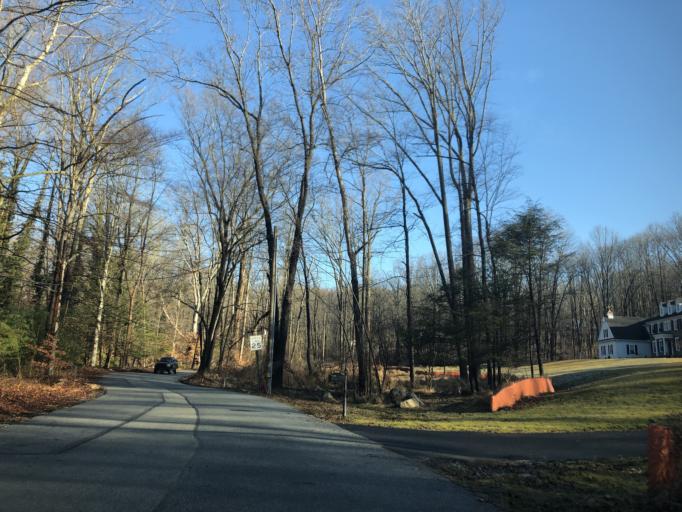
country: US
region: Pennsylvania
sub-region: Delaware County
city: Chester Heights
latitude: 39.9302
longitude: -75.4958
